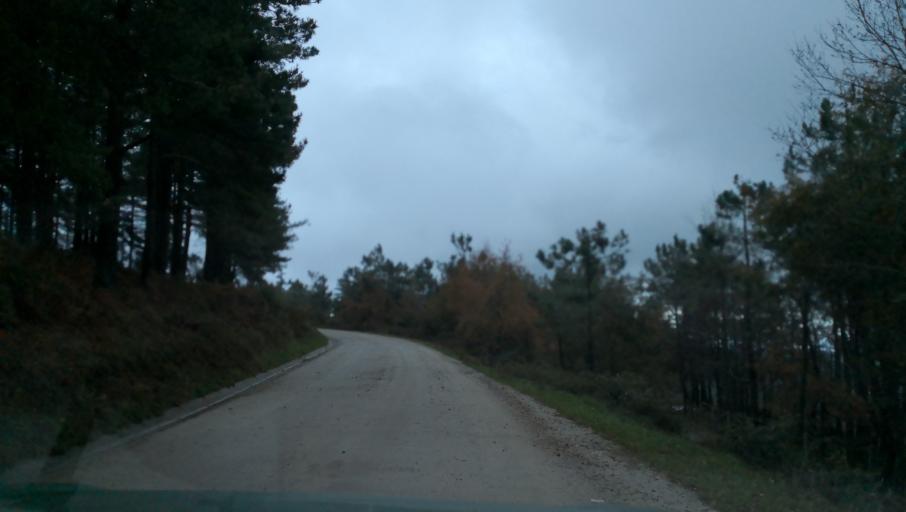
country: PT
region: Vila Real
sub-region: Mondim de Basto
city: Mondim de Basto
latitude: 41.3163
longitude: -7.8854
